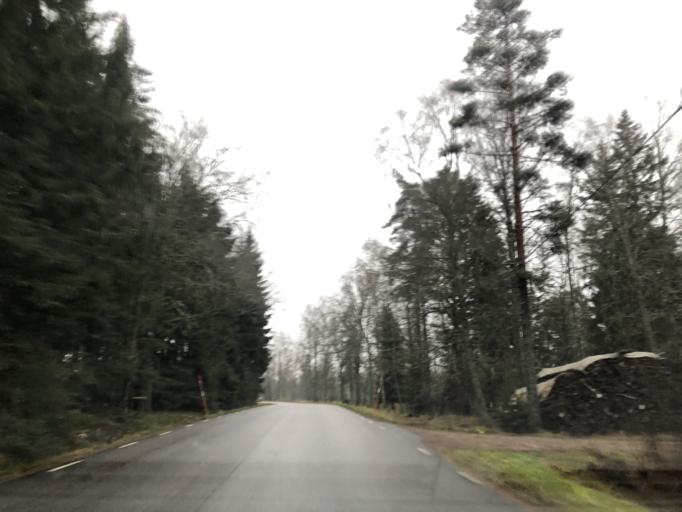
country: SE
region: Vaestra Goetaland
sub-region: Ulricehamns Kommun
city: Ulricehamn
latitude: 57.8513
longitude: 13.2567
